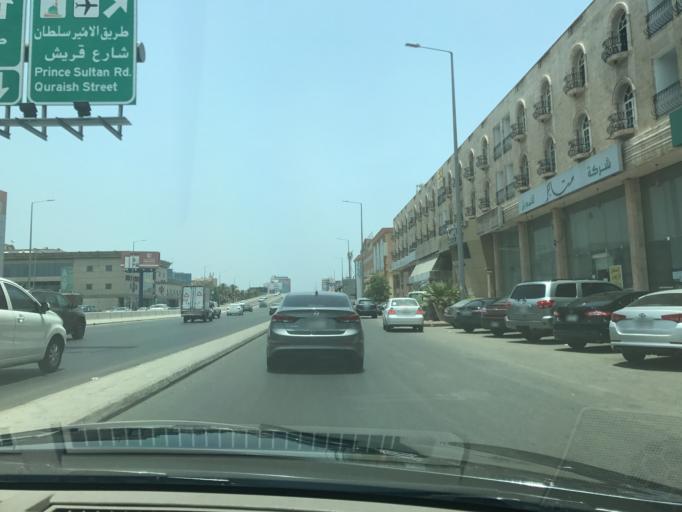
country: SA
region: Makkah
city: Jeddah
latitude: 21.5763
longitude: 39.1481
